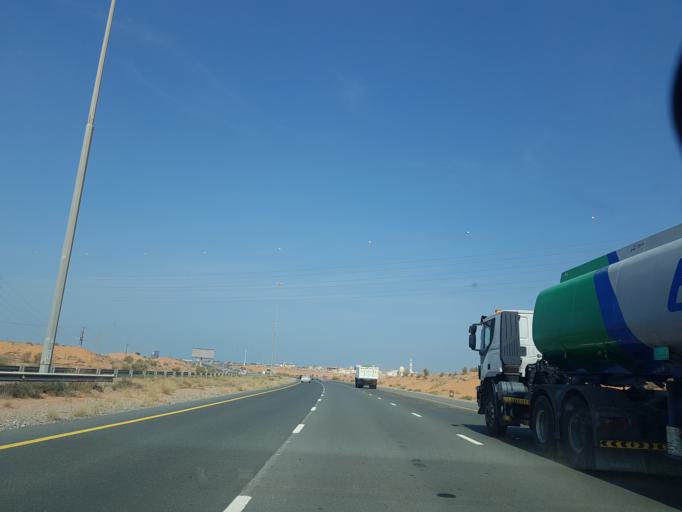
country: AE
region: Ra's al Khaymah
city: Ras al-Khaimah
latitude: 25.6838
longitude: 55.8830
